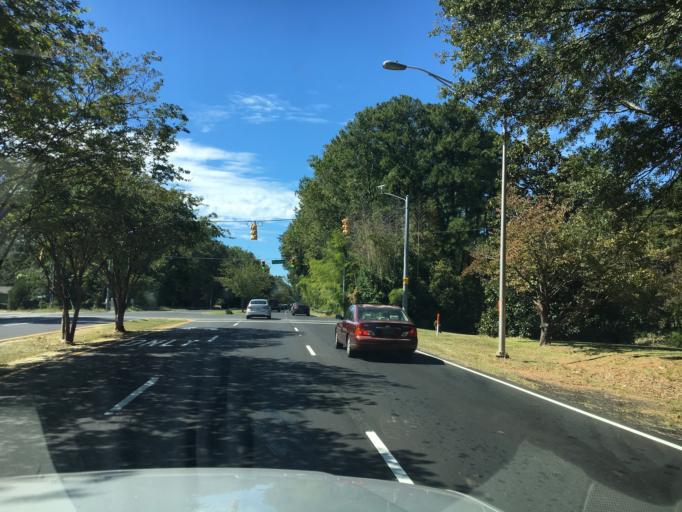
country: US
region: South Carolina
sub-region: Spartanburg County
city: Saxon
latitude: 34.9396
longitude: -81.9607
